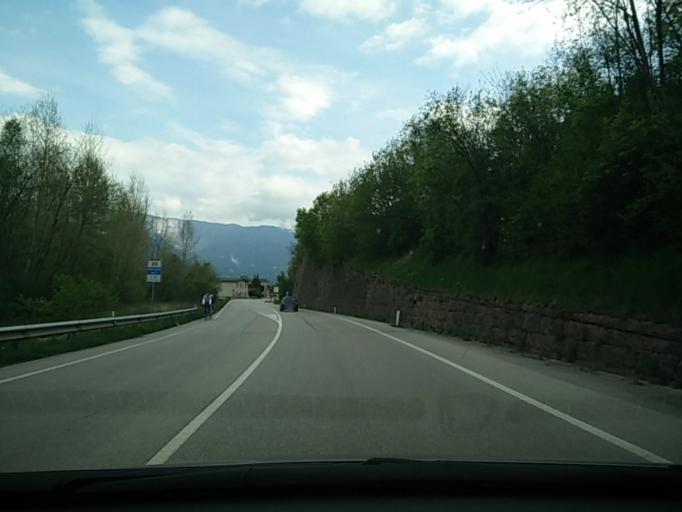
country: IT
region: Veneto
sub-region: Provincia di Belluno
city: Soccher-Paiane-Casan-Arsie
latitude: 46.1395
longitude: 12.3164
